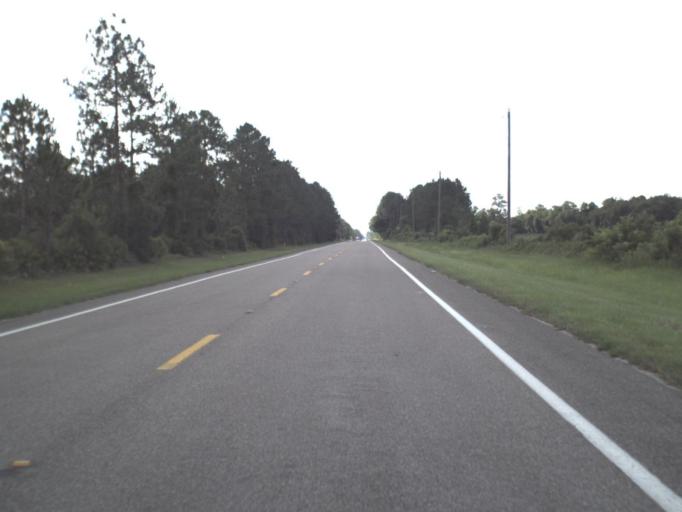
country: US
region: Florida
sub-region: Putnam County
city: East Palatka
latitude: 29.5687
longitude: -81.5478
